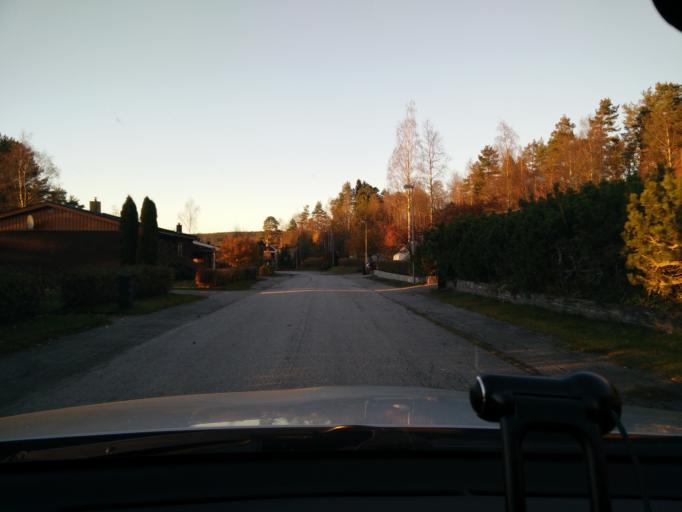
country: SE
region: Vaesternorrland
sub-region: Sundsvalls Kommun
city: Matfors
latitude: 62.3489
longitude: 17.0475
